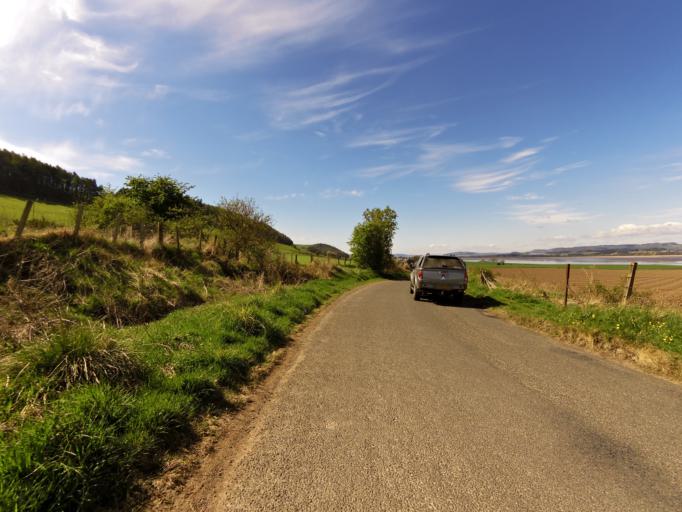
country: GB
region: Scotland
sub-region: Perth and Kinross
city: Errol
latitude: 56.3758
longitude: -3.1457
